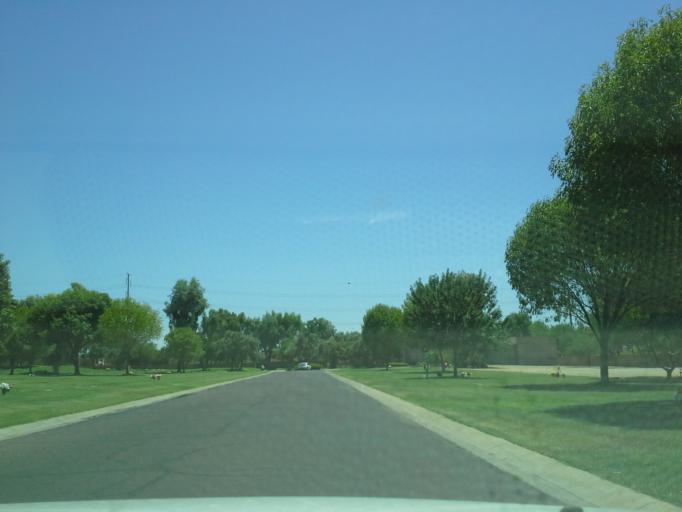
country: US
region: Arizona
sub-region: Maricopa County
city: Scottsdale
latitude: 33.5845
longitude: -111.8819
